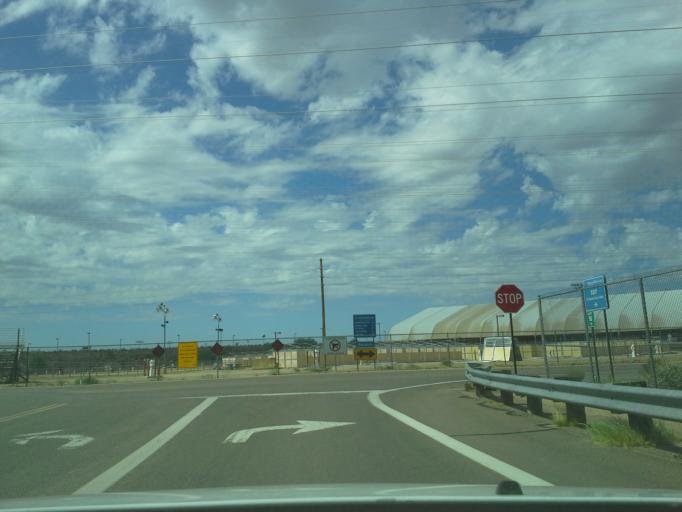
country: US
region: Arizona
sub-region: Maricopa County
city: Paradise Valley
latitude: 33.6304
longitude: -111.8715
